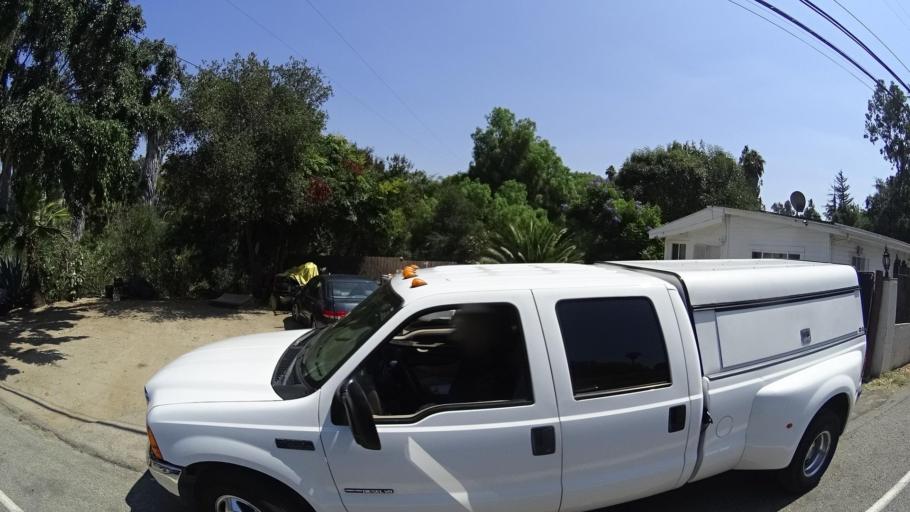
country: US
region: California
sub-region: San Diego County
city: Bonsall
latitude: 33.2485
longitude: -117.2289
